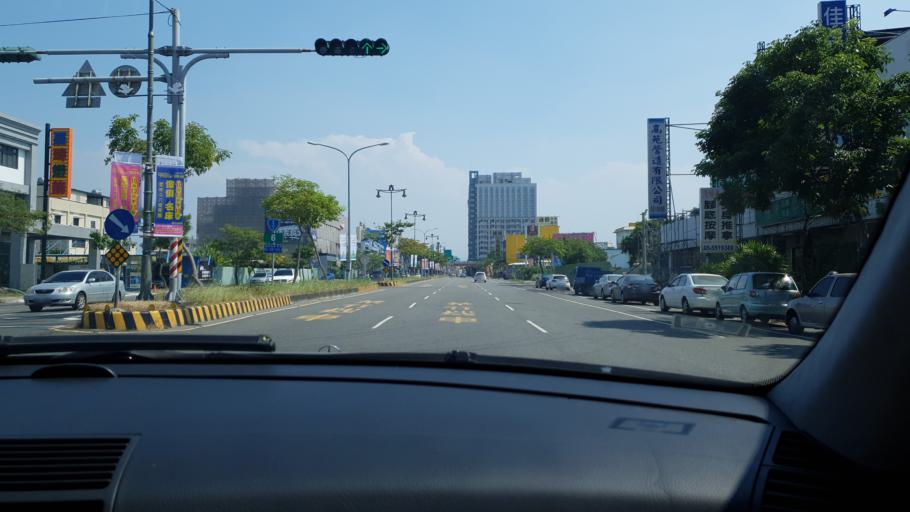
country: TW
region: Taiwan
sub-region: Yunlin
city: Douliu
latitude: 23.7157
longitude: 120.5304
